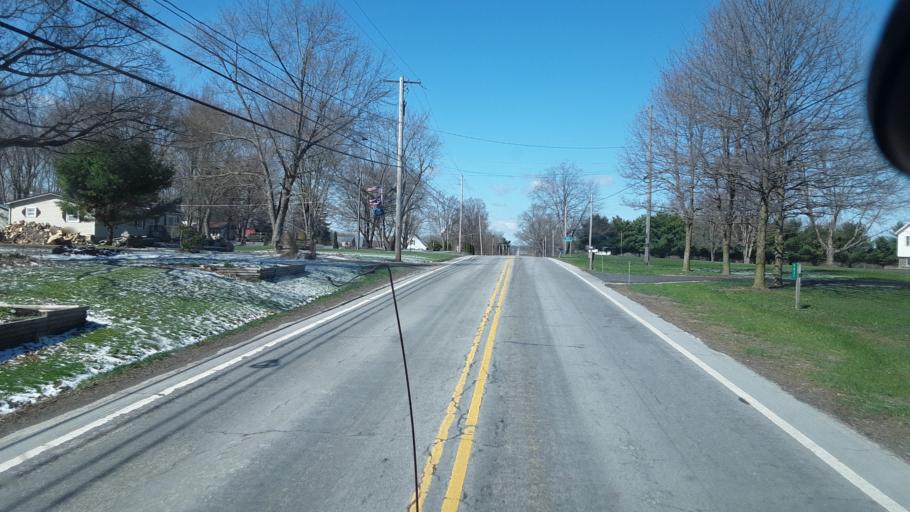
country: US
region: Ohio
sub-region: Ashtabula County
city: Andover
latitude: 41.6070
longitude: -80.6034
